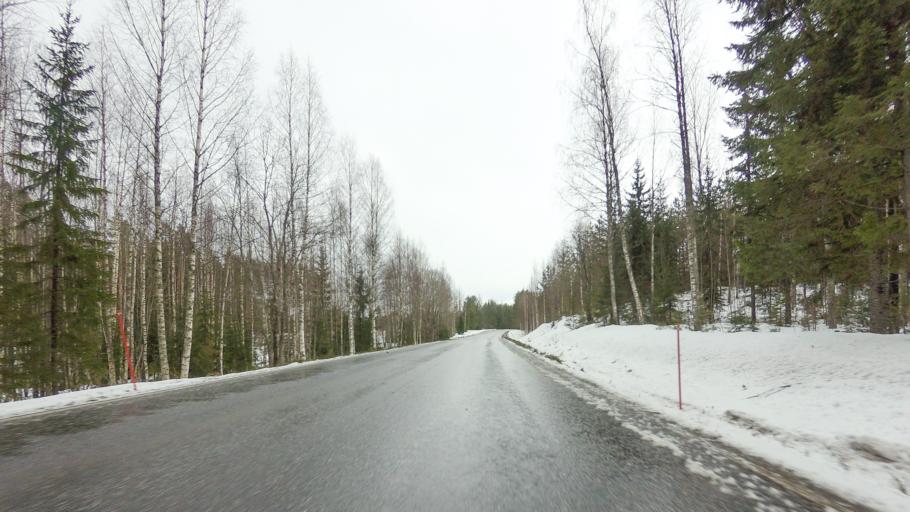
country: FI
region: Southern Savonia
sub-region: Savonlinna
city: Savonlinna
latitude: 61.9750
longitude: 28.8162
